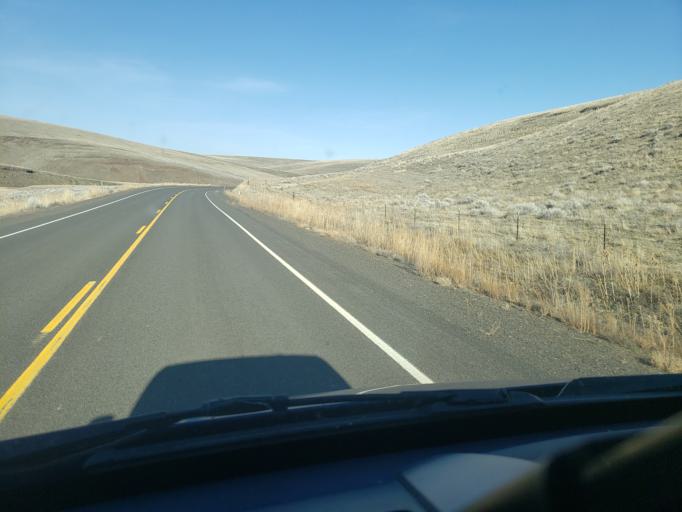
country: US
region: Oregon
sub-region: Umatilla County
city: Pilot Rock
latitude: 45.4646
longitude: -118.9256
